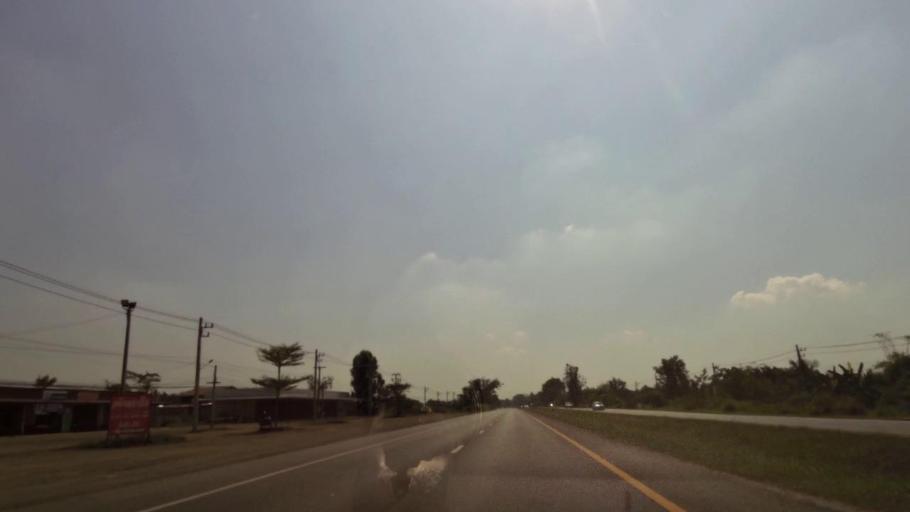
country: TH
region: Phichit
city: Bueng Na Rang
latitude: 16.2487
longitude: 100.1254
